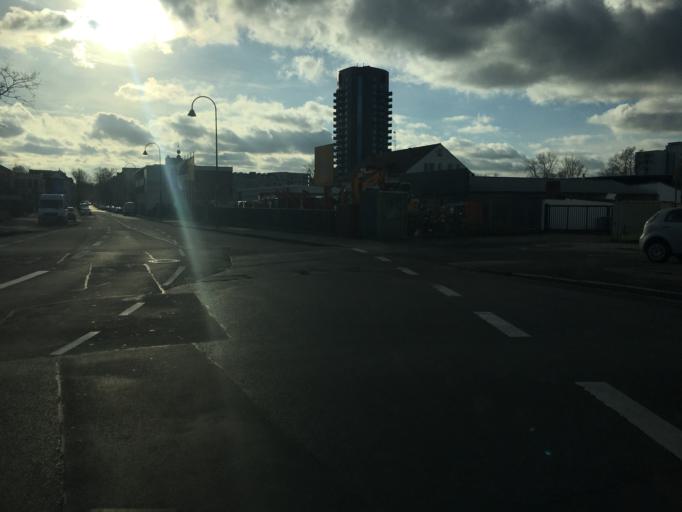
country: DE
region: North Rhine-Westphalia
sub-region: Regierungsbezirk Koln
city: Muelheim
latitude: 50.9795
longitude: 7.0021
